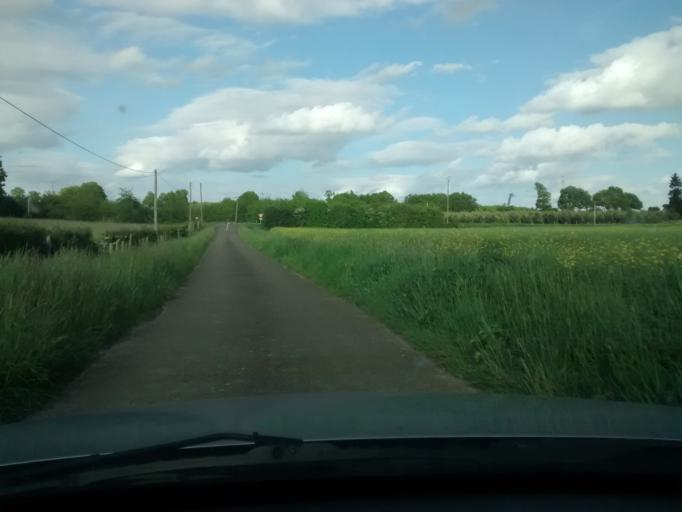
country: FR
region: Pays de la Loire
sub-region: Departement de la Sarthe
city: Challes
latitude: 47.9525
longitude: 0.4592
